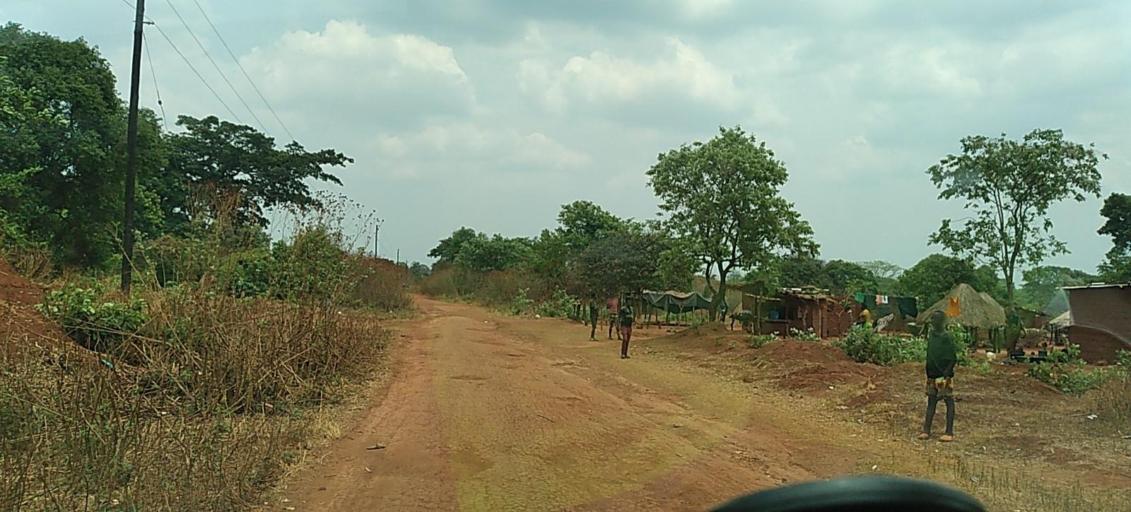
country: ZM
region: North-Western
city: Kansanshi
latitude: -12.0394
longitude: 26.3985
